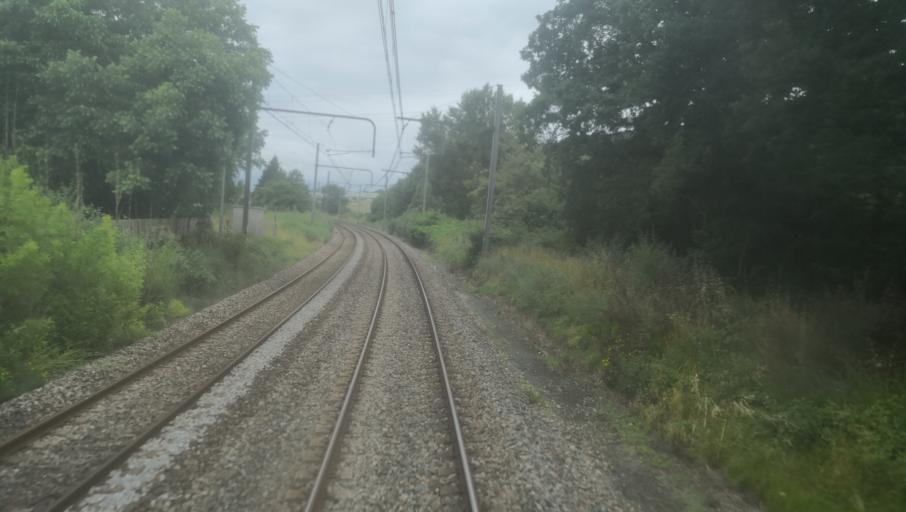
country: FR
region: Aquitaine
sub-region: Departement du Lot-et-Garonne
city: Port-Sainte-Marie
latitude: 44.2416
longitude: 0.4569
